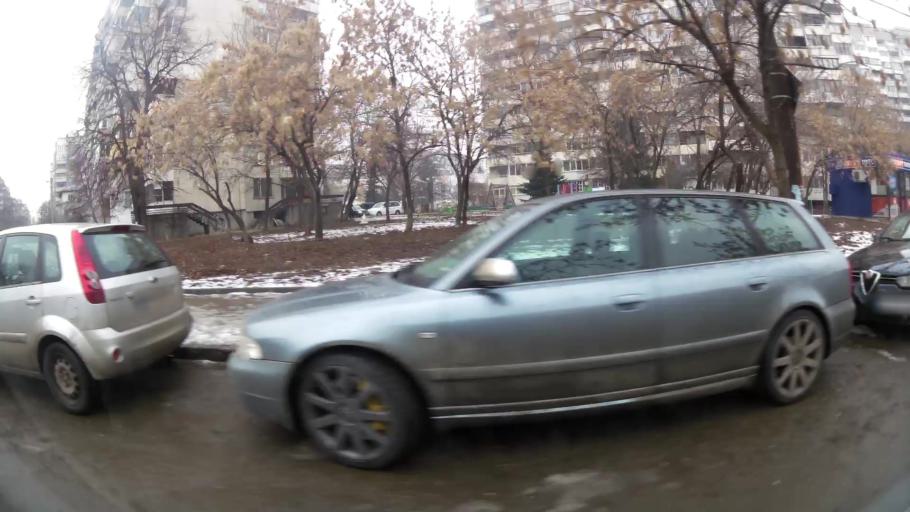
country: BG
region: Sofia-Capital
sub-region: Stolichna Obshtina
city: Sofia
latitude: 42.6791
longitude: 23.2912
